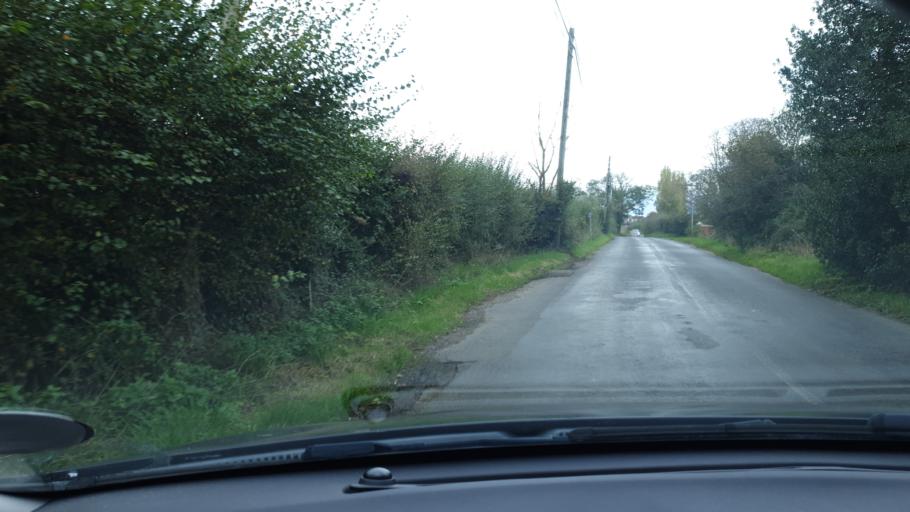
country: GB
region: England
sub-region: Essex
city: Mistley
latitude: 51.9368
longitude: 1.0948
